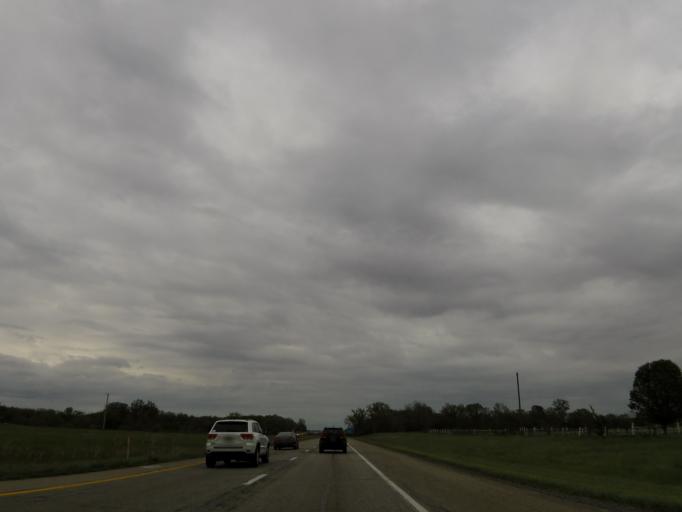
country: US
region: Ohio
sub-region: Madison County
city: Bethel
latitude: 39.7458
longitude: -83.3293
